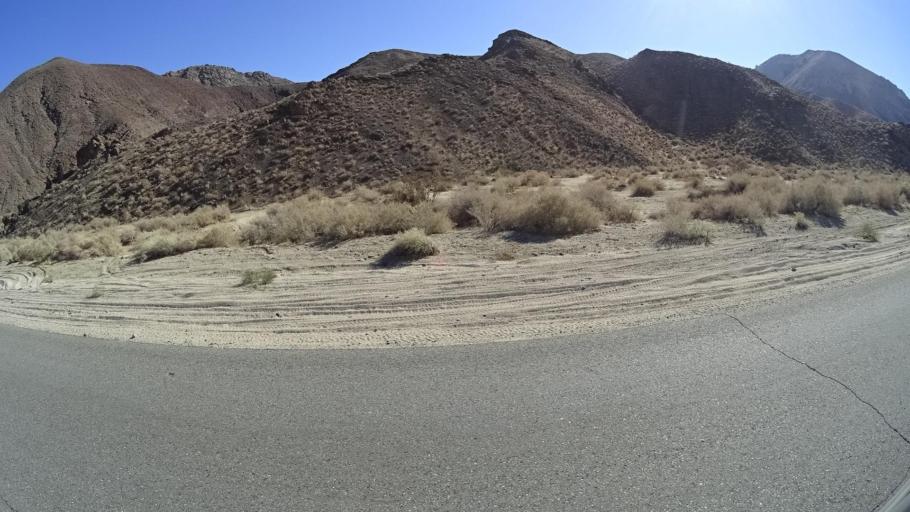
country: US
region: California
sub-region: Kern County
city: California City
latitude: 35.3150
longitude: -118.0879
